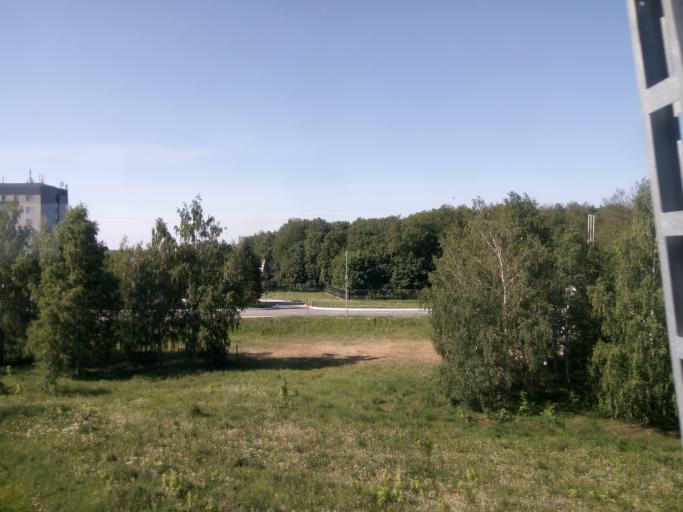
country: RU
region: Tatarstan
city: Stolbishchi
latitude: 55.6122
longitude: 49.2918
